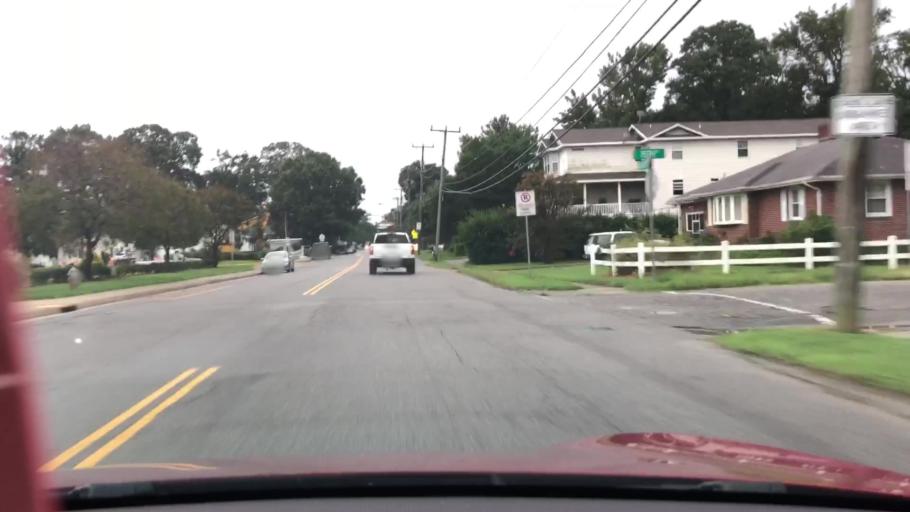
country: US
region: Virginia
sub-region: City of Virginia Beach
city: Virginia Beach
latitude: 36.8424
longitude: -75.9806
